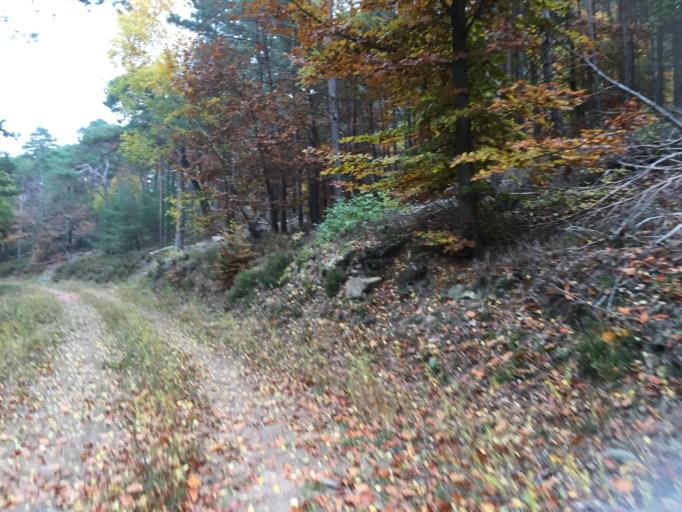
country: DE
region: Rheinland-Pfalz
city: Wachenheim
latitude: 49.4203
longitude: 8.1424
